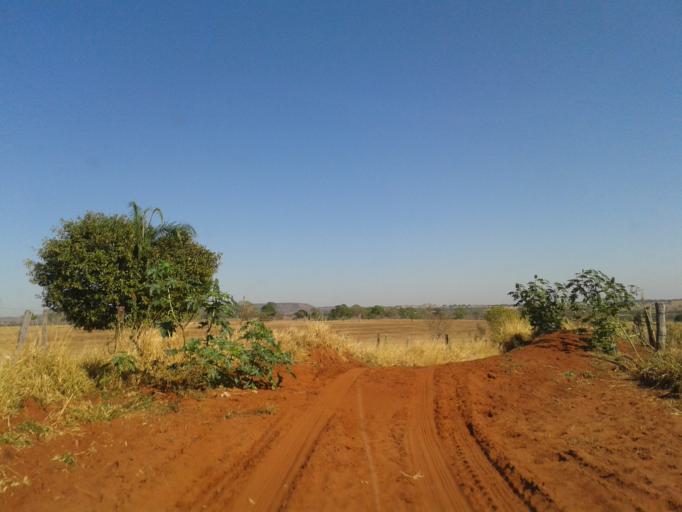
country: BR
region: Minas Gerais
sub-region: Santa Vitoria
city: Santa Vitoria
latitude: -19.0463
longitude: -49.9462
